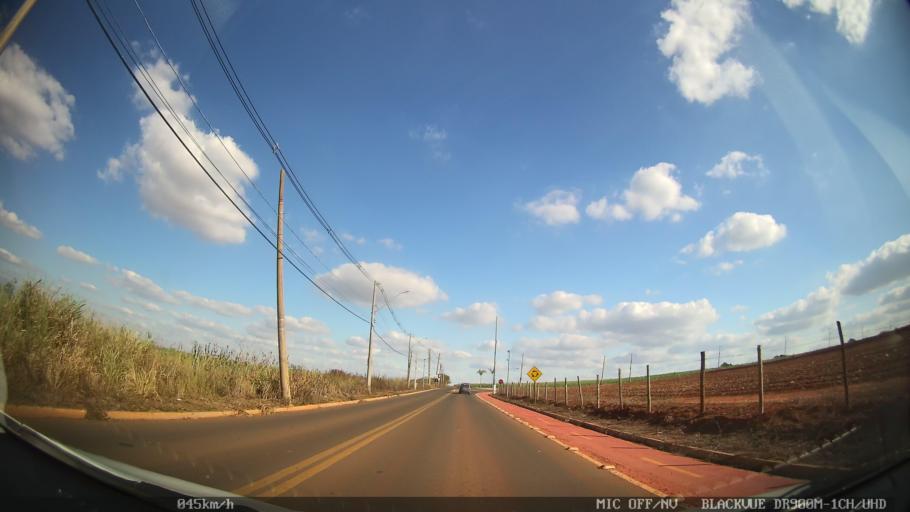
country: BR
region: Sao Paulo
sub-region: Nova Odessa
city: Nova Odessa
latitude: -22.8147
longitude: -47.3229
